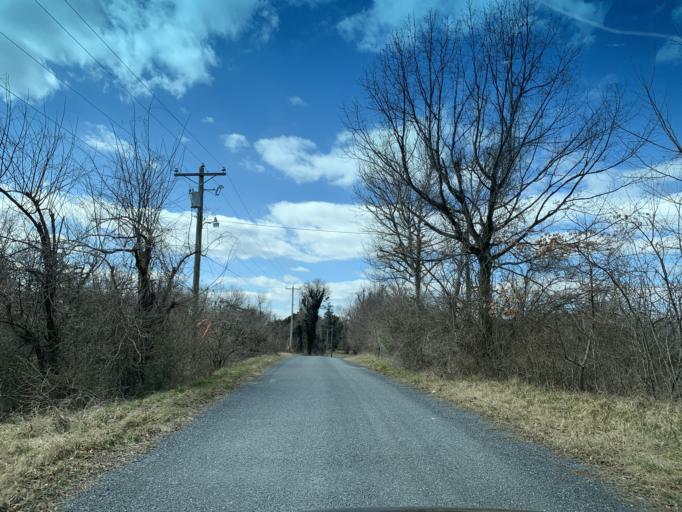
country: US
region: Maryland
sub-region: Queen Anne's County
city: Stevensville
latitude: 39.0329
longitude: -76.3070
